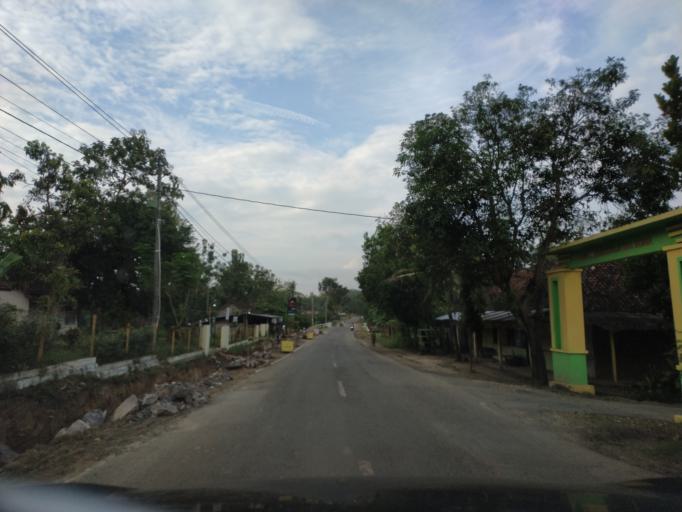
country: ID
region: Central Java
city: Medang
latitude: -6.9069
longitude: 111.4409
